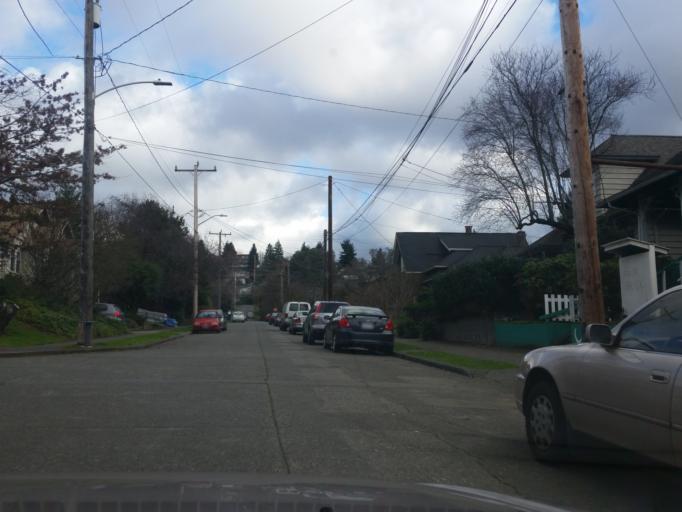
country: US
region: Washington
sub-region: King County
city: Seattle
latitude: 47.6578
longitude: -122.3632
